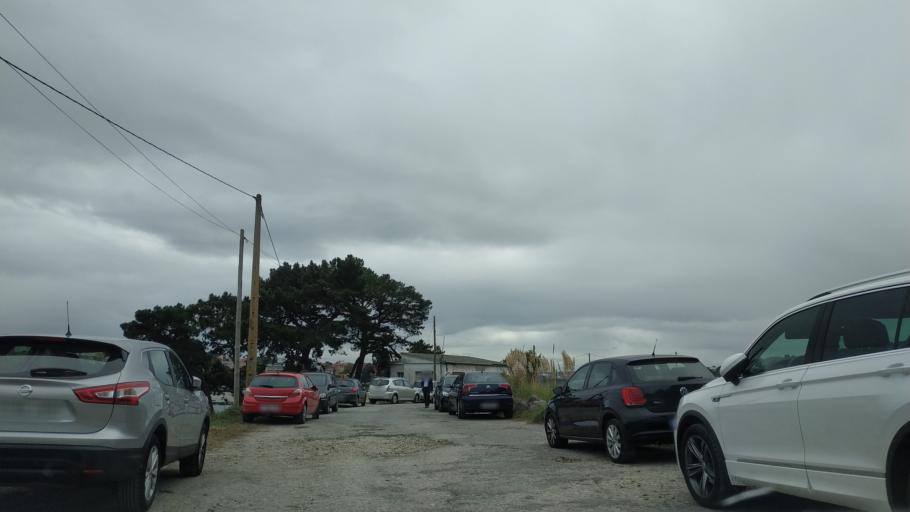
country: ES
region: Galicia
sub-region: Provincia da Coruna
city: A Coruna
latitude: 43.3393
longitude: -8.3871
